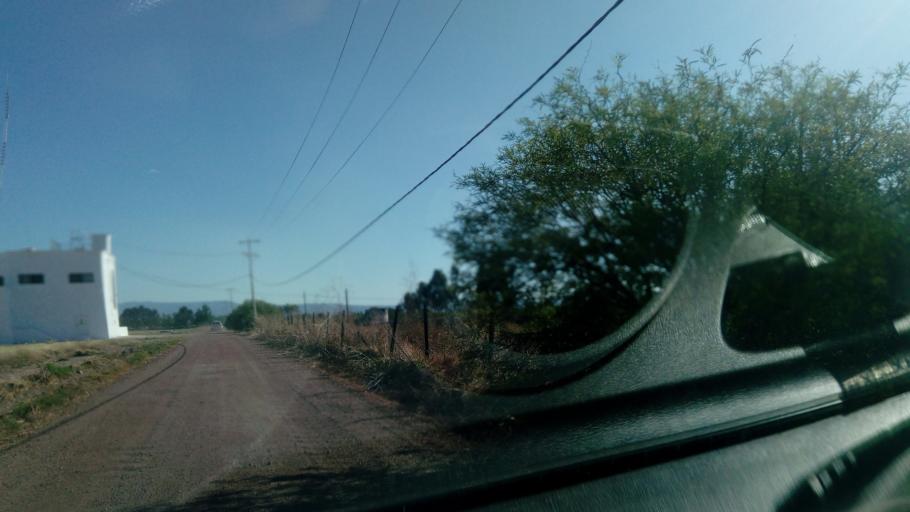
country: MX
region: Durango
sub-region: Durango
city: Jose Refugio Salcido
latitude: 24.0168
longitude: -104.5535
